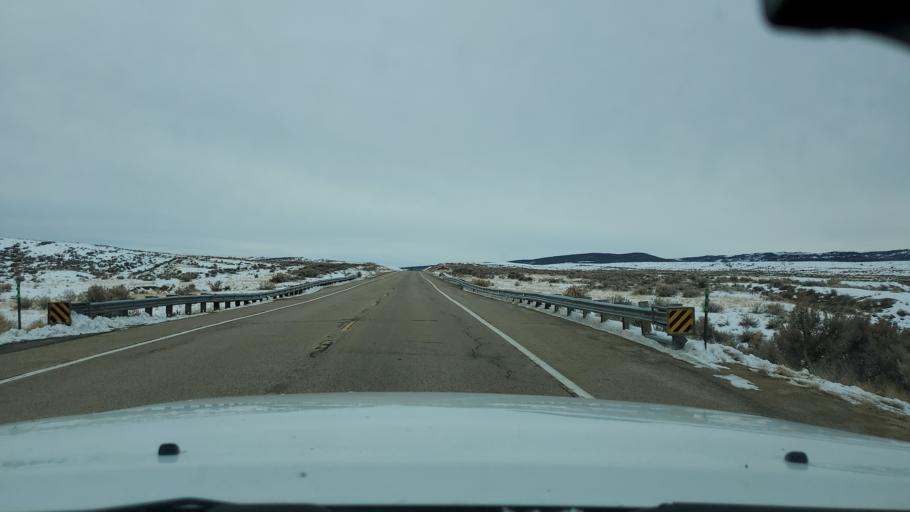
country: US
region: Colorado
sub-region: Rio Blanco County
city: Rangely
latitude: 40.2948
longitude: -108.5353
